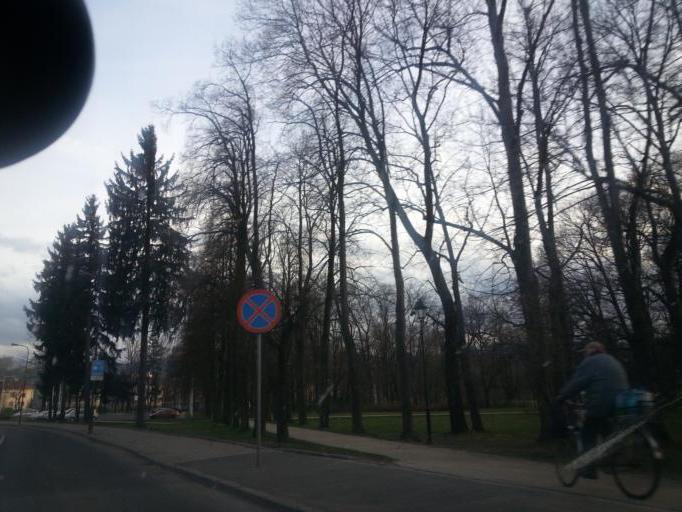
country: PL
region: Lower Silesian Voivodeship
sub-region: Jelenia Gora
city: Cieplice Slaskie Zdroj
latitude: 50.8576
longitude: 15.6820
